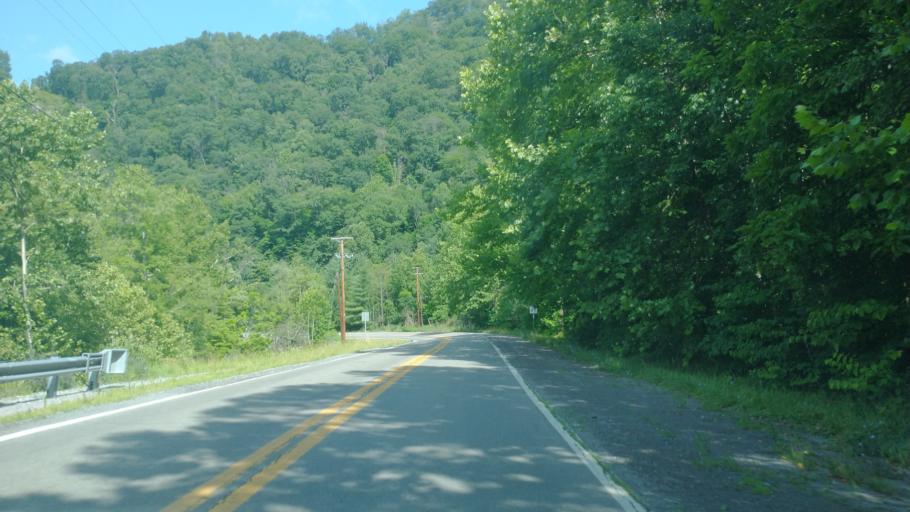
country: US
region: West Virginia
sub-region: McDowell County
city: Welch
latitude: 37.4142
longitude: -81.5240
